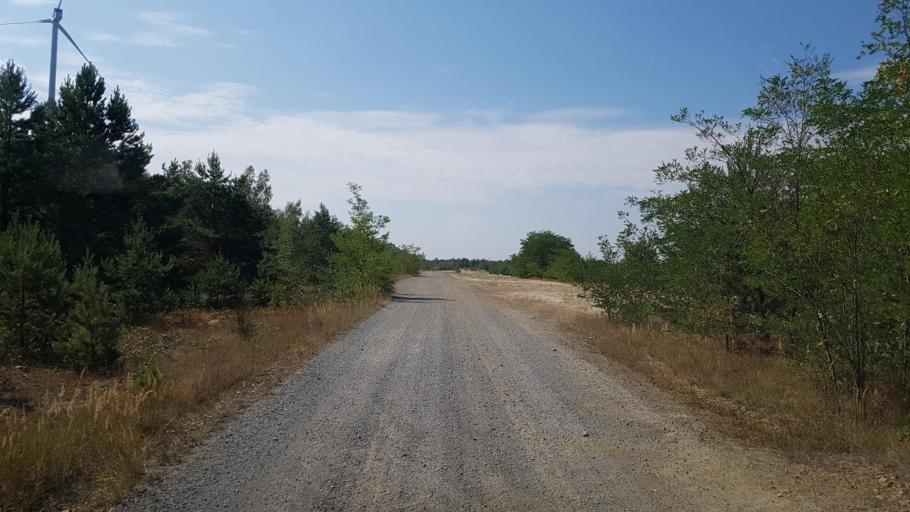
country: DE
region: Brandenburg
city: Schipkau
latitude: 51.5358
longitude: 13.8620
